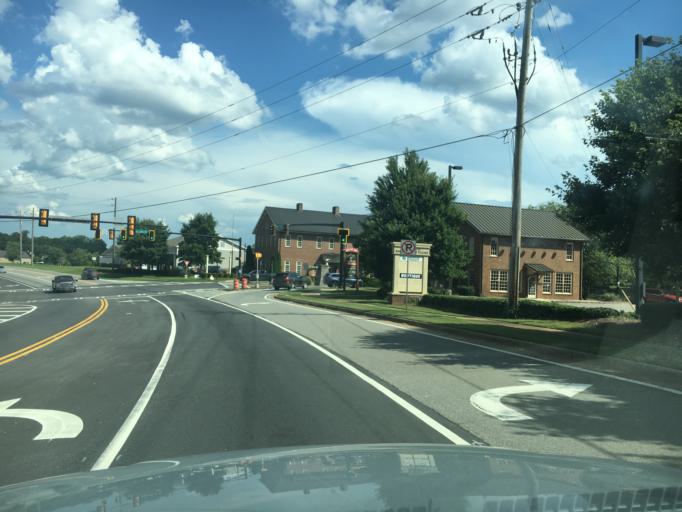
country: US
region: Georgia
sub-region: Cherokee County
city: Holly Springs
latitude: 34.1955
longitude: -84.4491
